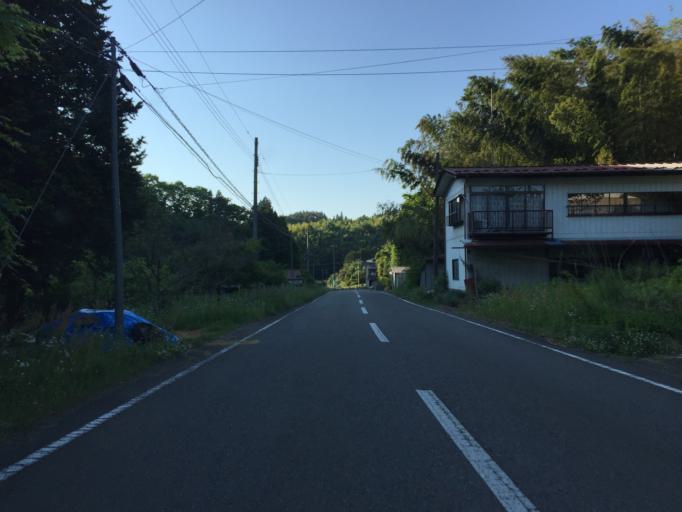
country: JP
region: Ibaraki
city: Daigo
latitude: 36.9226
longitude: 140.4593
